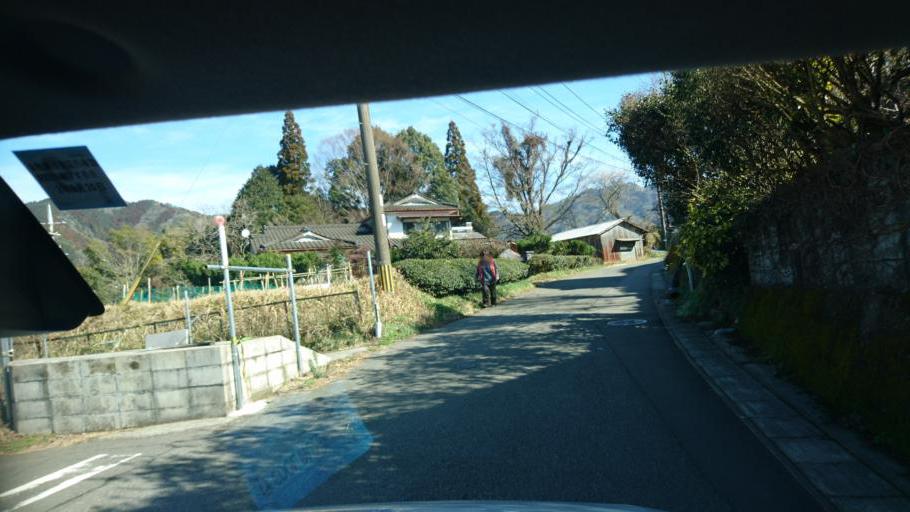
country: JP
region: Oita
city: Takedamachi
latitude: 32.6858
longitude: 131.3499
